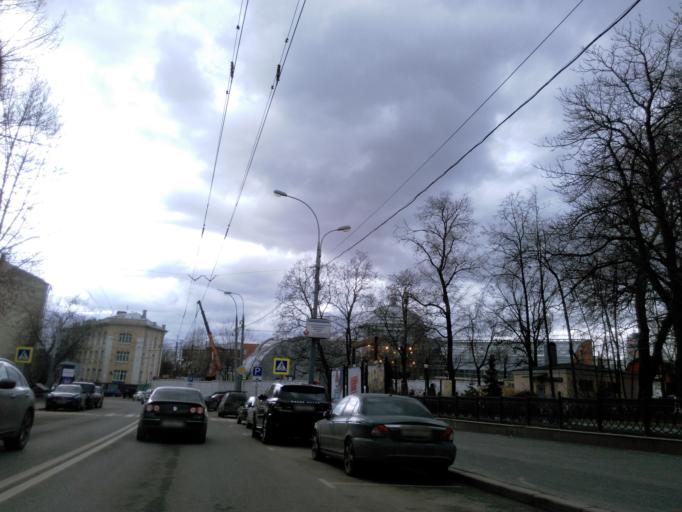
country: RU
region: Moskovskaya
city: Dorogomilovo
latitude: 55.7661
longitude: 37.5782
